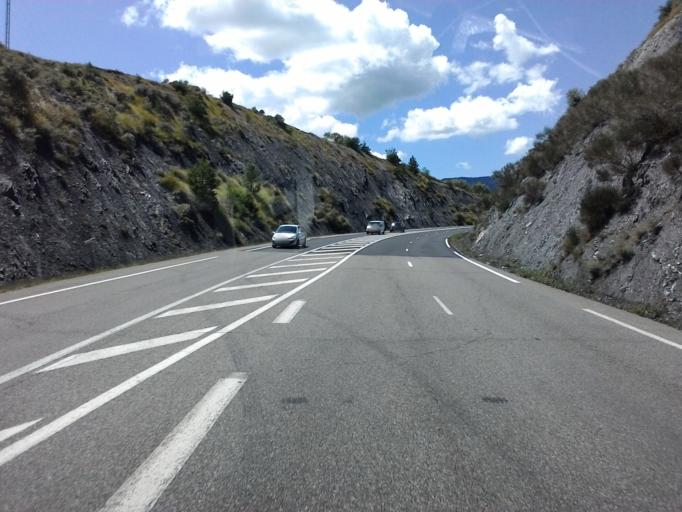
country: FR
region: Provence-Alpes-Cote d'Azur
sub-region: Departement des Hautes-Alpes
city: Chorges
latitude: 44.5300
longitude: 6.3215
